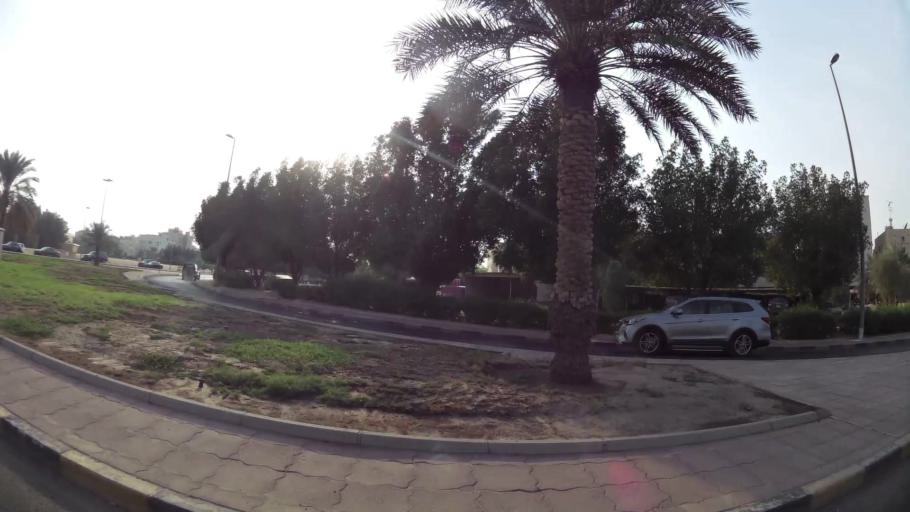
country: KW
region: Mubarak al Kabir
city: Mubarak al Kabir
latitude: 29.2087
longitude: 48.0688
